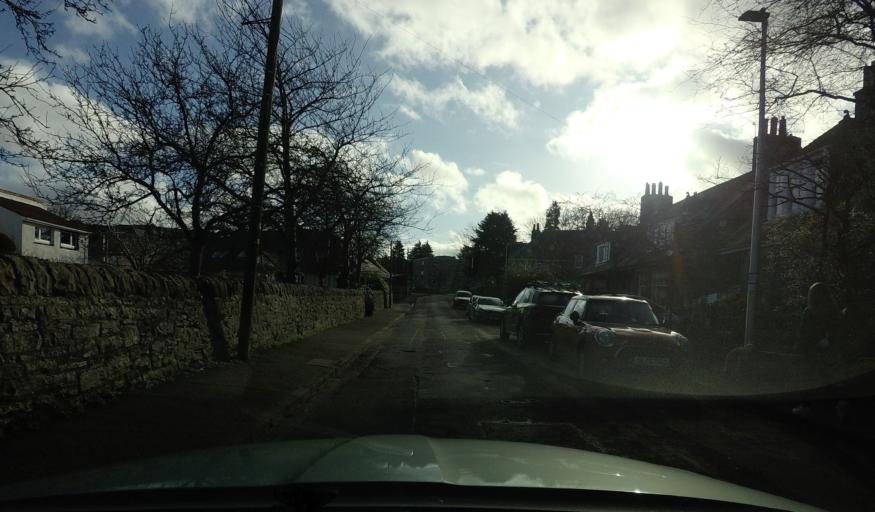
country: GB
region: Scotland
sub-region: Fife
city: Aberdour
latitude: 55.9760
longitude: -3.2996
